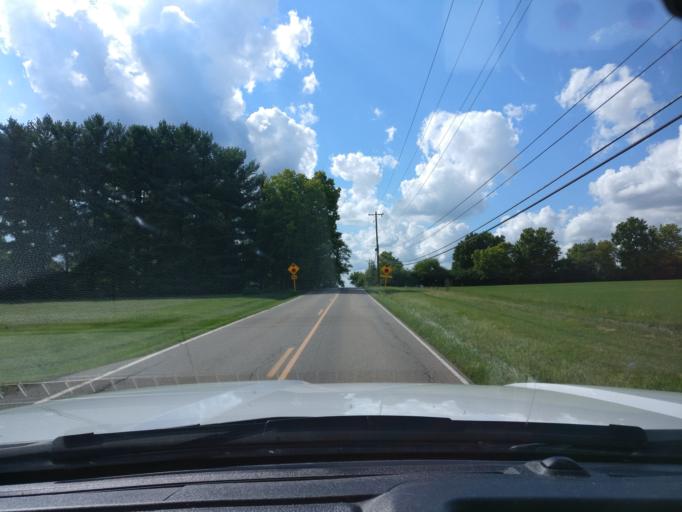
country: US
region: Ohio
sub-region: Warren County
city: Springboro
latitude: 39.5074
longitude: -84.2366
